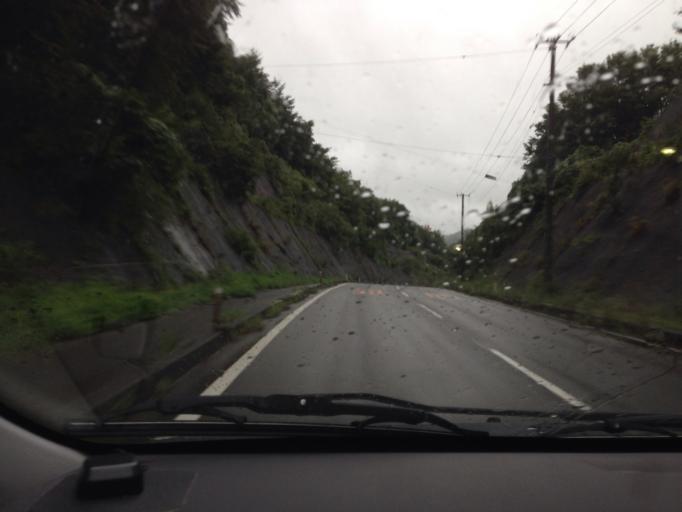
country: JP
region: Fukushima
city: Koriyama
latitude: 37.4106
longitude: 140.2701
